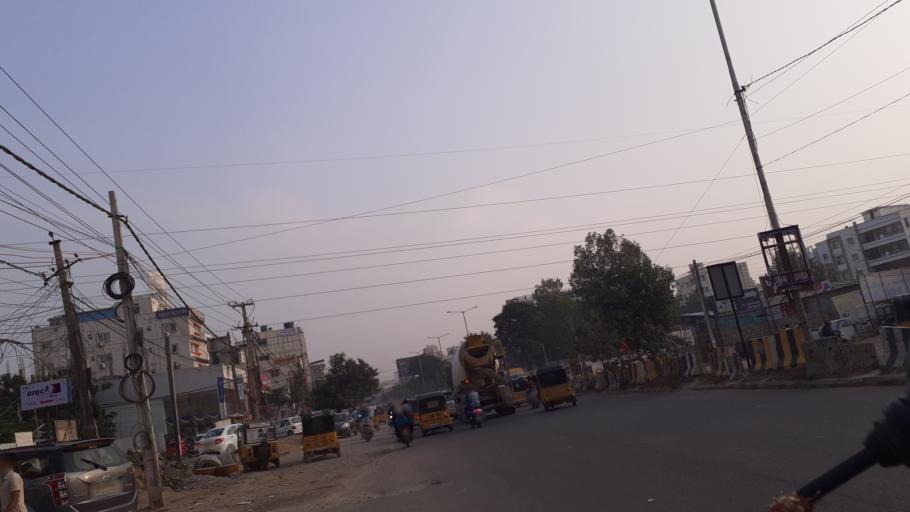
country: IN
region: Telangana
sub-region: Rangareddi
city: Kukatpalli
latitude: 17.4712
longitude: 78.3651
